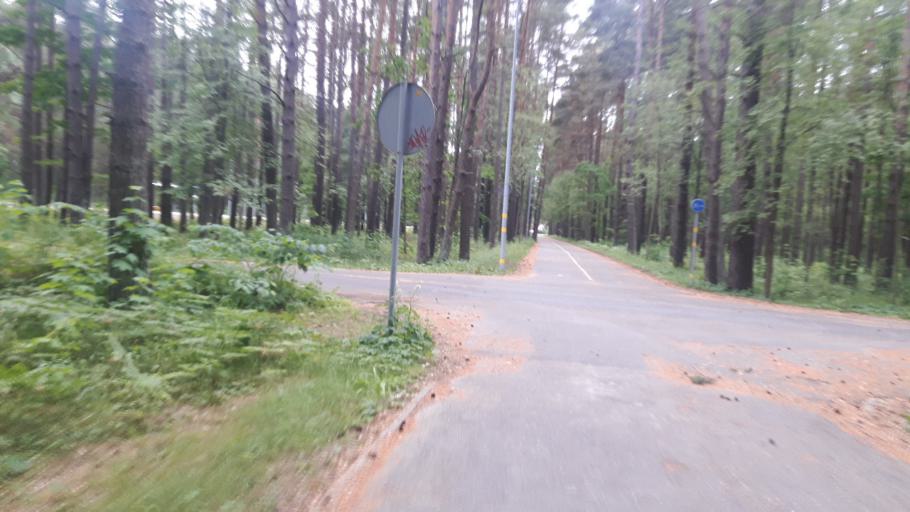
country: LV
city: Tireli
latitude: 56.9575
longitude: 23.6362
